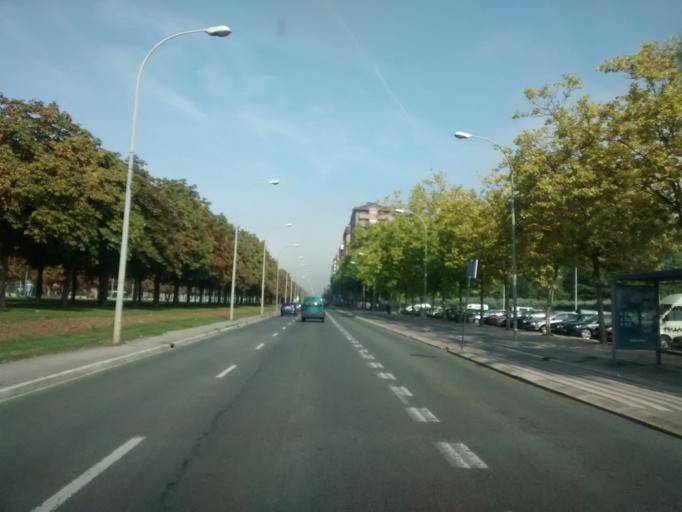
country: ES
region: Basque Country
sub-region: Provincia de Alava
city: Gasteiz / Vitoria
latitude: 42.8600
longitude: -2.6819
